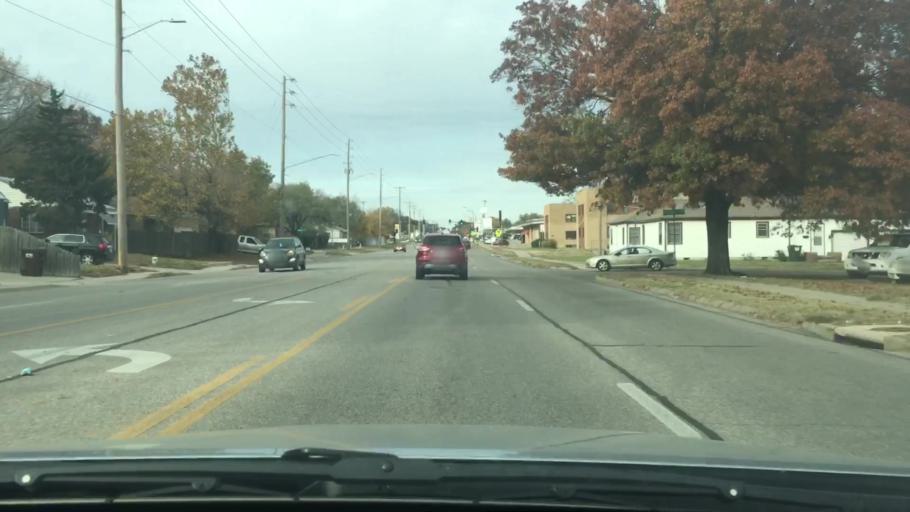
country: US
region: Kansas
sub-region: Sedgwick County
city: Wichita
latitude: 37.6748
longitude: -97.2805
